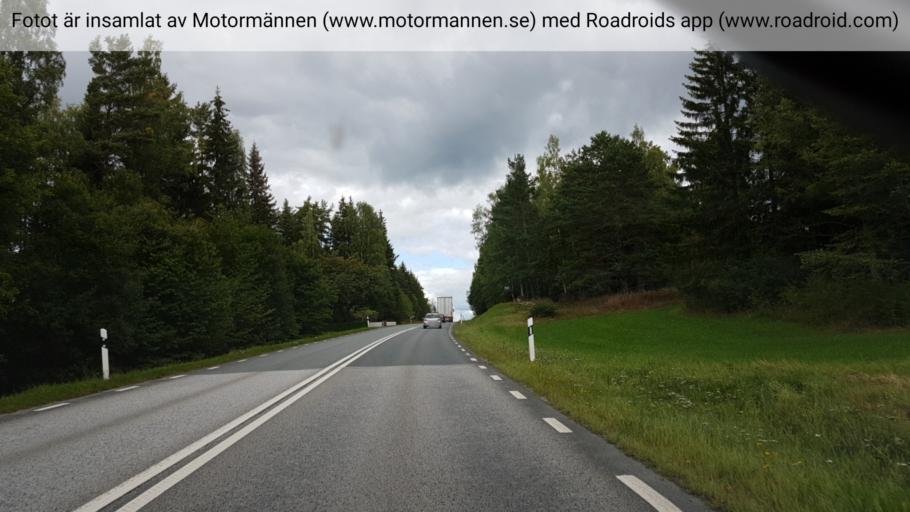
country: SE
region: Joenkoeping
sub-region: Tranas Kommun
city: Tranas
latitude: 57.9340
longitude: 14.9124
